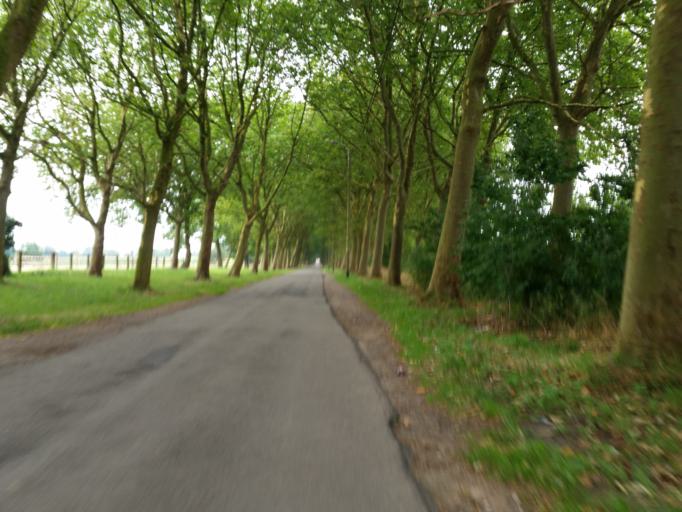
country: BE
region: Flanders
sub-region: Provincie Vlaams-Brabant
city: Kapelle-op-den-Bos
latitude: 51.0039
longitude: 4.4078
